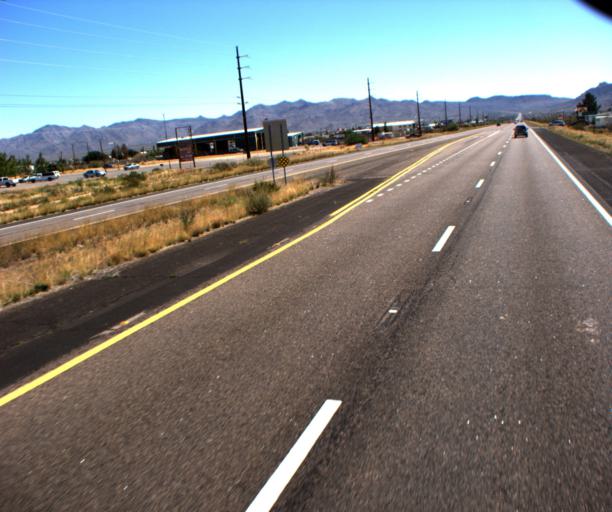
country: US
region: Arizona
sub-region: Mohave County
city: Golden Valley
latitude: 35.2221
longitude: -114.2204
